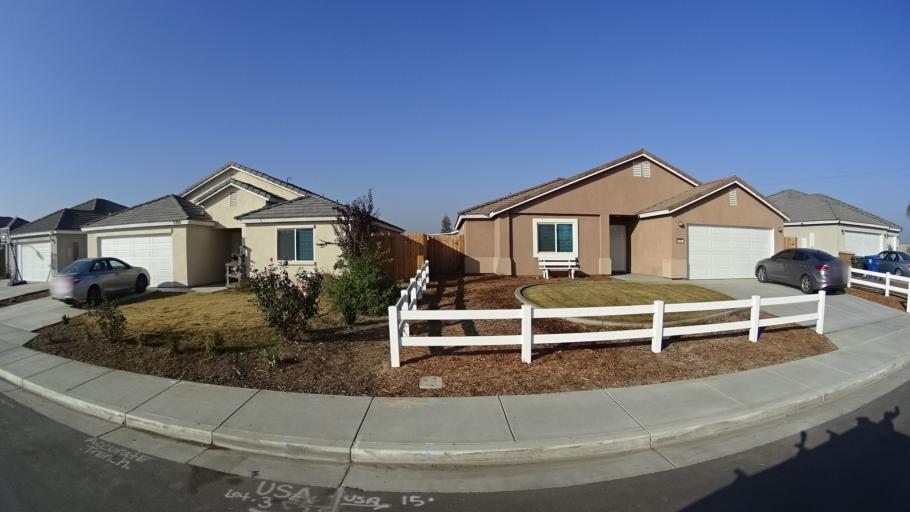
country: US
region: California
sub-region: Kern County
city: Greenfield
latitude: 35.2663
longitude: -119.0144
